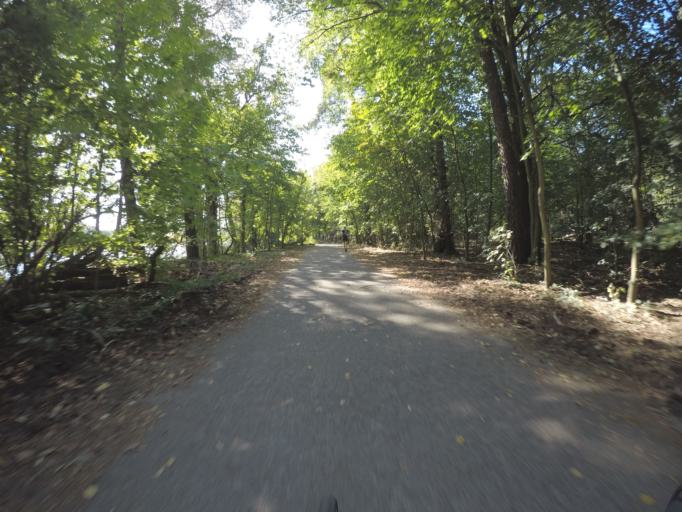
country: DE
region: Berlin
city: Konradshohe
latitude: 52.5731
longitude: 13.2399
